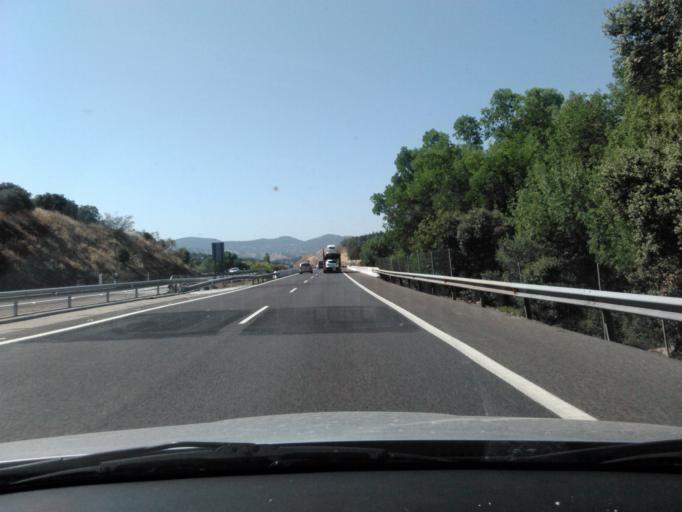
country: ES
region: Castille-La Mancha
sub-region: Provincia de Ciudad Real
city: Viso del Marques
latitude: 38.4499
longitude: -3.4970
